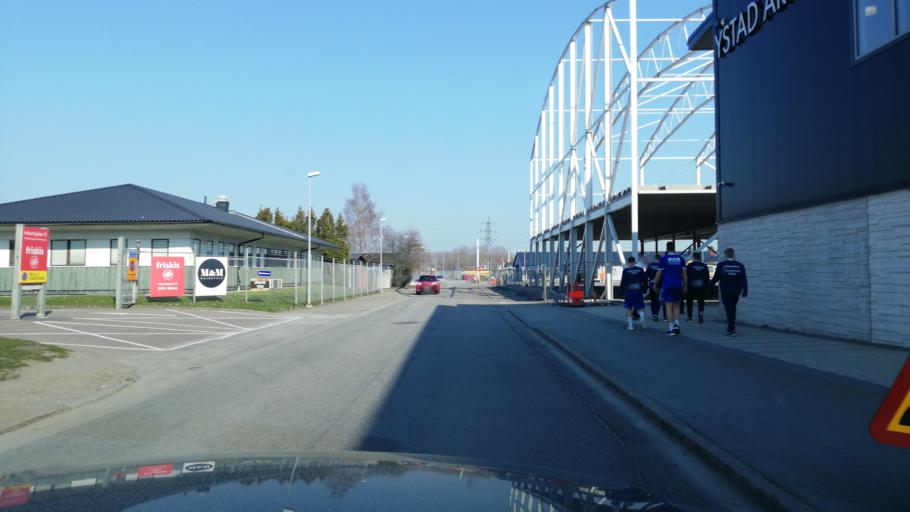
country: SE
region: Skane
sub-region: Ystads Kommun
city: Ystad
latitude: 55.4346
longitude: 13.8326
